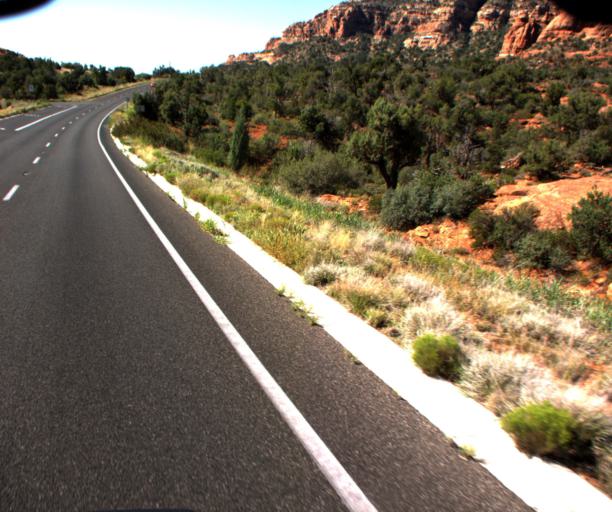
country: US
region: Arizona
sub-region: Yavapai County
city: Village of Oak Creek (Big Park)
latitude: 34.8063
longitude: -111.7683
